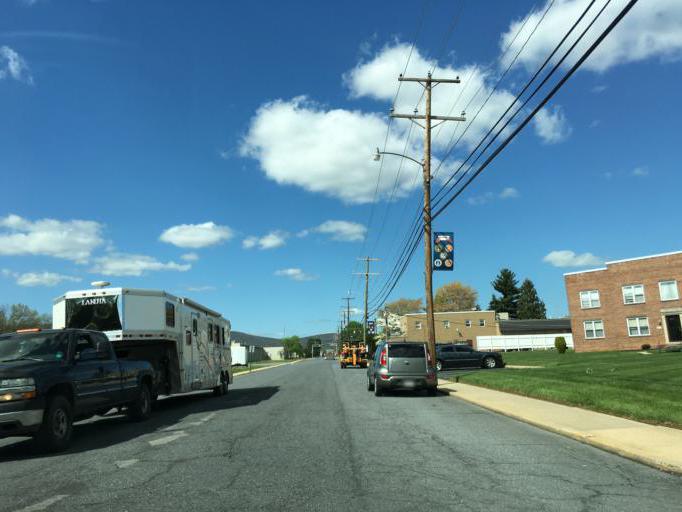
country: US
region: Maryland
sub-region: Frederick County
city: Thurmont
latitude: 39.6212
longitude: -77.4006
